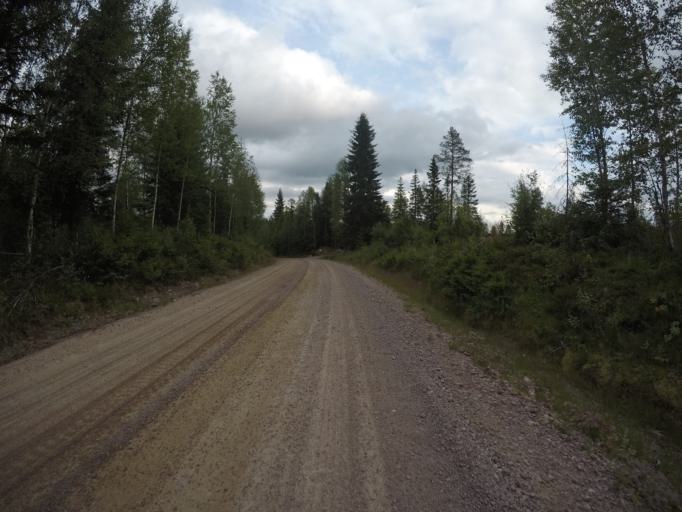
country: SE
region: Vaermland
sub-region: Filipstads Kommun
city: Lesjofors
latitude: 60.1759
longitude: 14.4020
